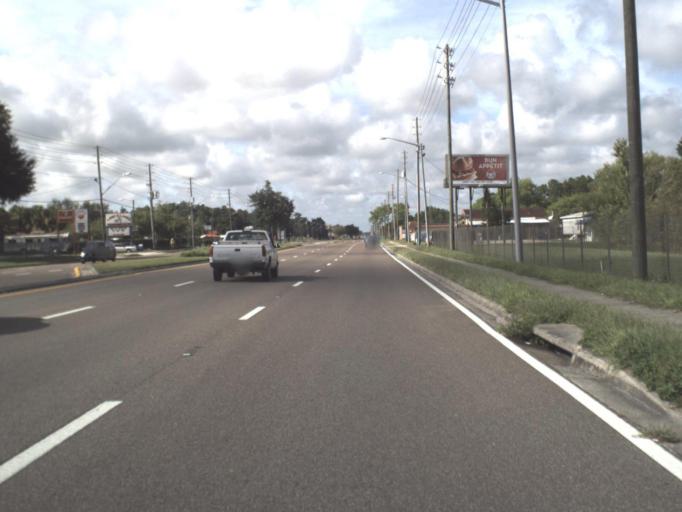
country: US
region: Florida
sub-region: Pasco County
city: Land O' Lakes
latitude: 28.2121
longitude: -82.4615
